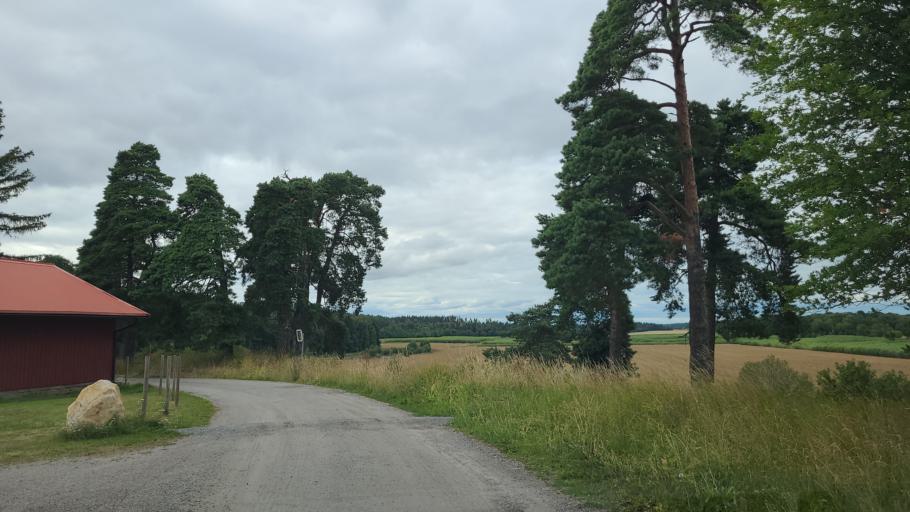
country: SE
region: Uppsala
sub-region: Habo Kommun
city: Balsta
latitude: 59.5105
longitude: 17.5651
